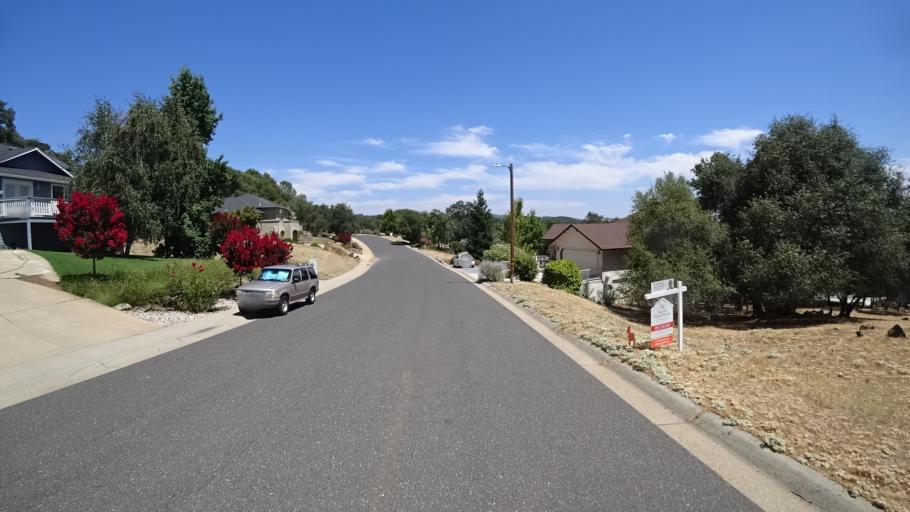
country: US
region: California
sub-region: Calaveras County
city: Angels Camp
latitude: 38.0732
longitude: -120.5629
